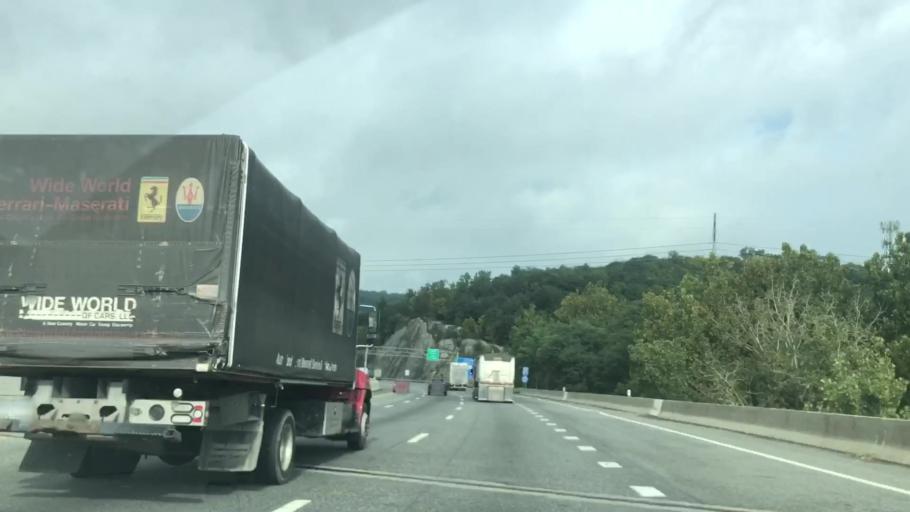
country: US
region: New York
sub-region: Rockland County
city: Sloatsburg
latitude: 41.1400
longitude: -74.1705
